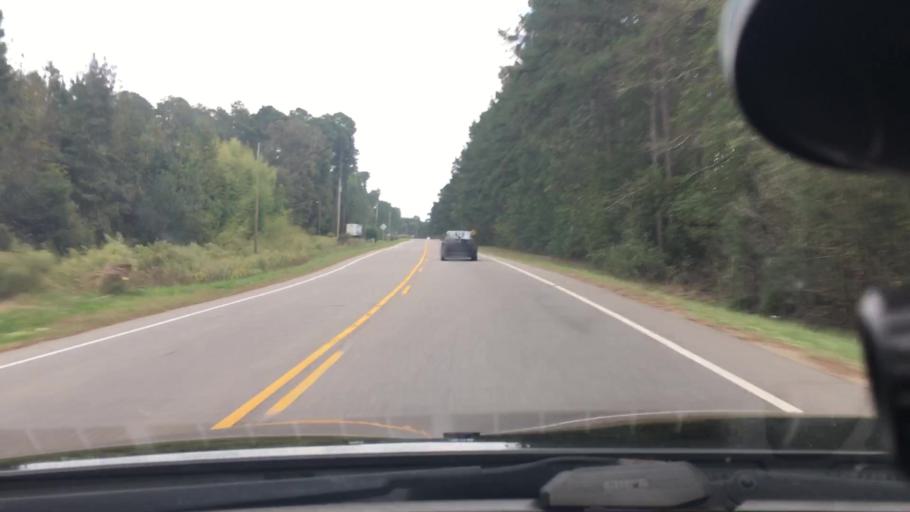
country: US
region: North Carolina
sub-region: Moore County
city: Carthage
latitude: 35.3781
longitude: -79.4728
